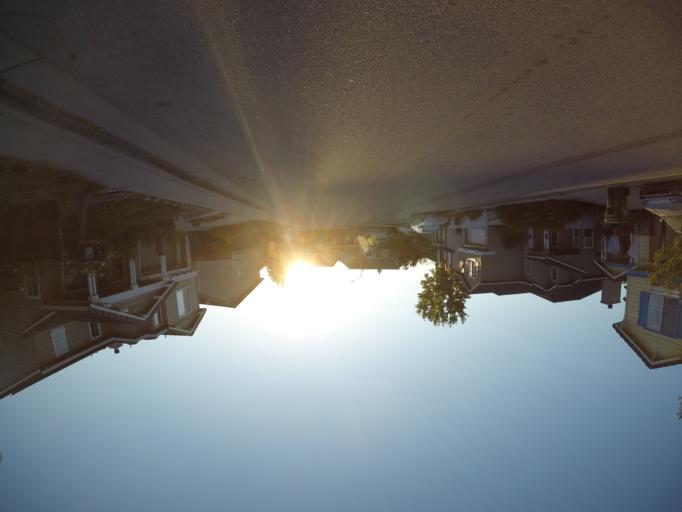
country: US
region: California
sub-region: Santa Cruz County
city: Scotts Valley
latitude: 37.0500
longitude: -122.0334
